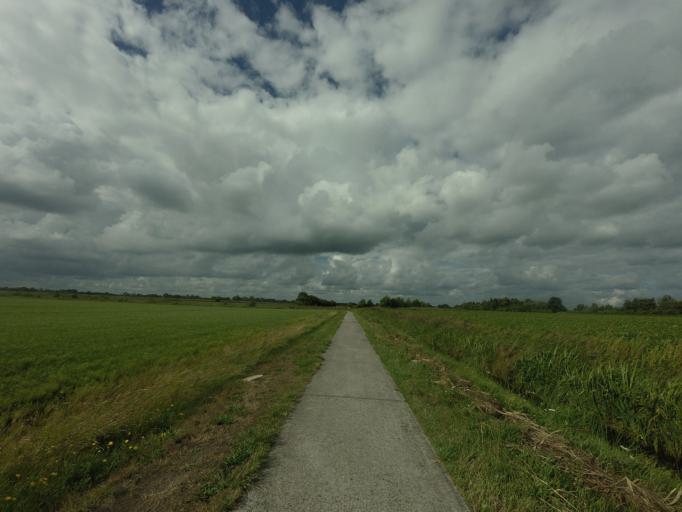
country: NL
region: Overijssel
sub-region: Gemeente Steenwijkerland
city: Wanneperveen
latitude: 52.7088
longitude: 6.1023
